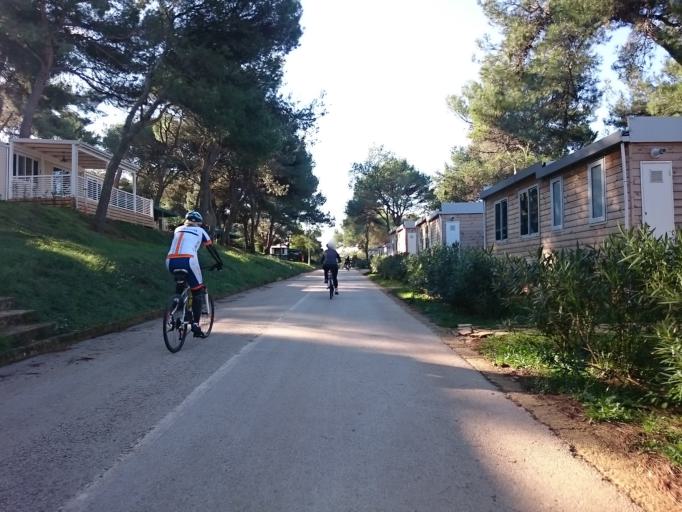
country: HR
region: Istarska
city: Novigrad
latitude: 45.3043
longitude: 13.5910
